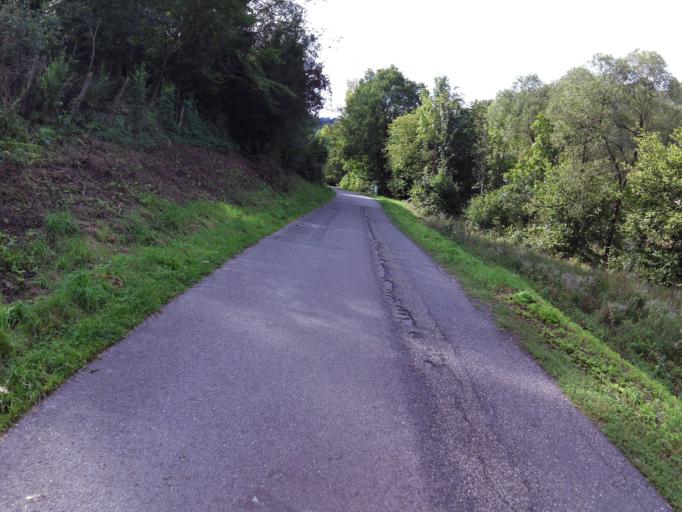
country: DE
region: Baden-Wuerttemberg
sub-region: Freiburg Region
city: Oberndorf
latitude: 48.3184
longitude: 8.5794
